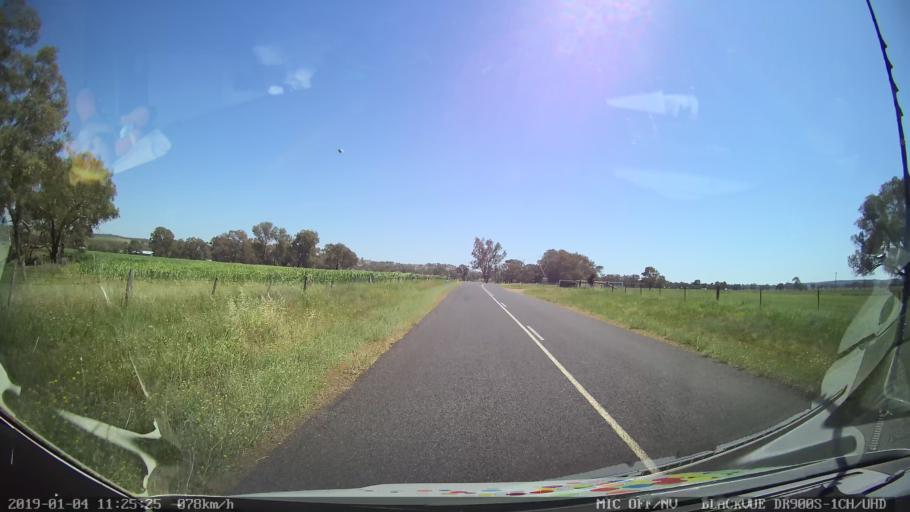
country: AU
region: New South Wales
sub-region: Cabonne
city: Molong
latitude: -33.1251
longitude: 148.7523
